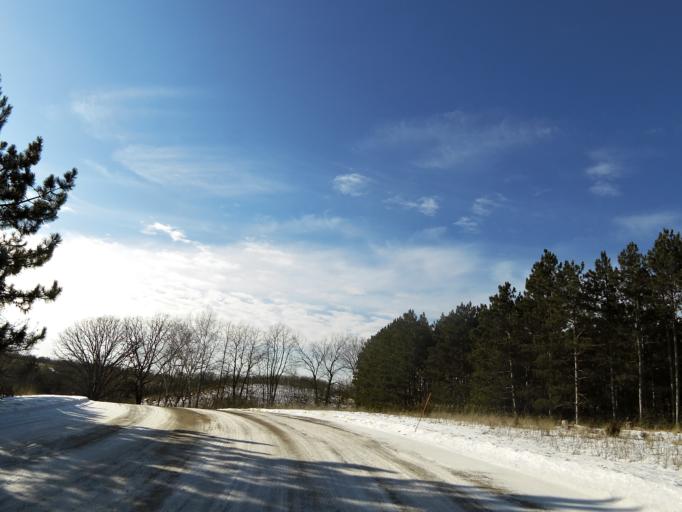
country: US
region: Wisconsin
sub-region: Saint Croix County
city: North Hudson
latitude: 45.0118
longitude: -92.6856
